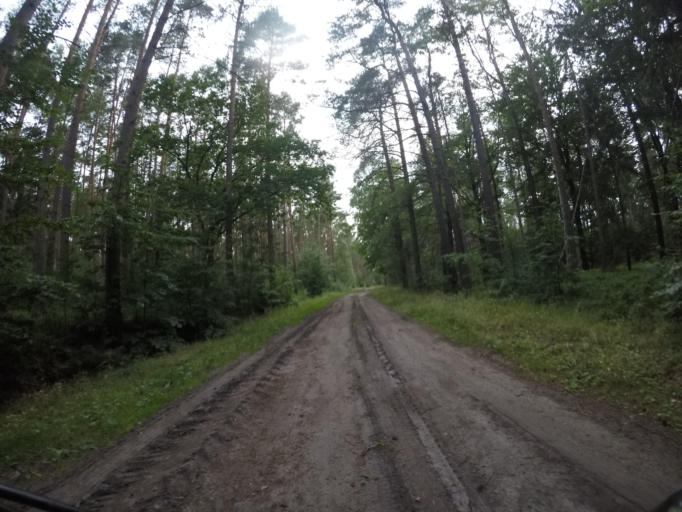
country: DE
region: Mecklenburg-Vorpommern
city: Lubtheen
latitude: 53.2503
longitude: 11.0205
